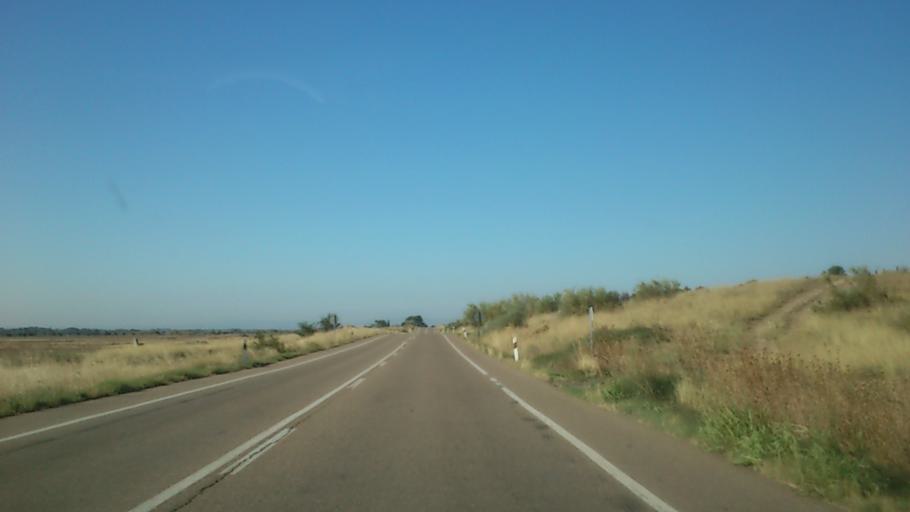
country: ES
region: Aragon
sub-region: Provincia de Zaragoza
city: Villanueva de Gallego
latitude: 41.8080
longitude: -0.8073
